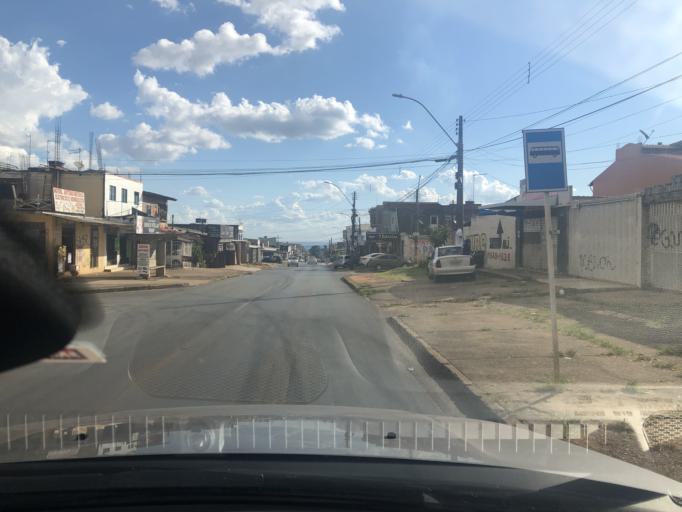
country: BR
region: Federal District
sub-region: Brasilia
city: Brasilia
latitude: -15.9191
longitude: -48.0567
